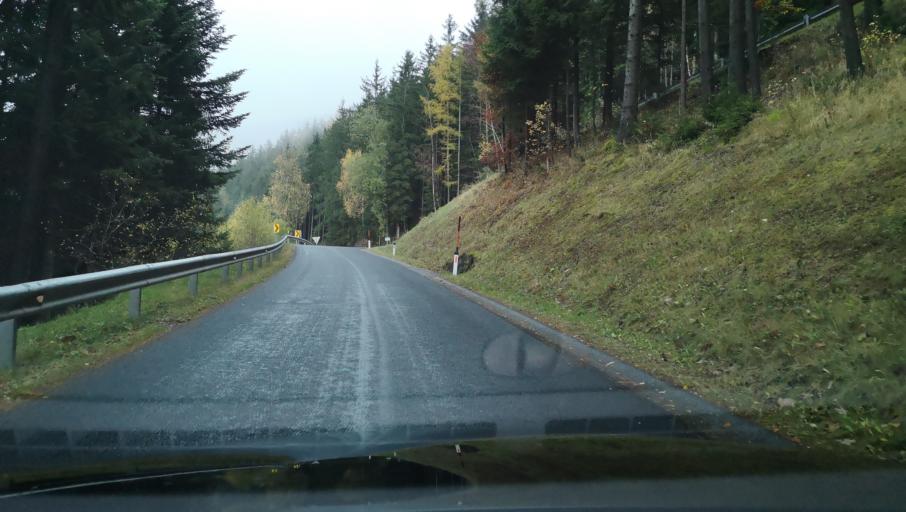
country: AT
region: Styria
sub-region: Politischer Bezirk Weiz
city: Sankt Kathrein am Offenegg
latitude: 47.3443
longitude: 15.6221
